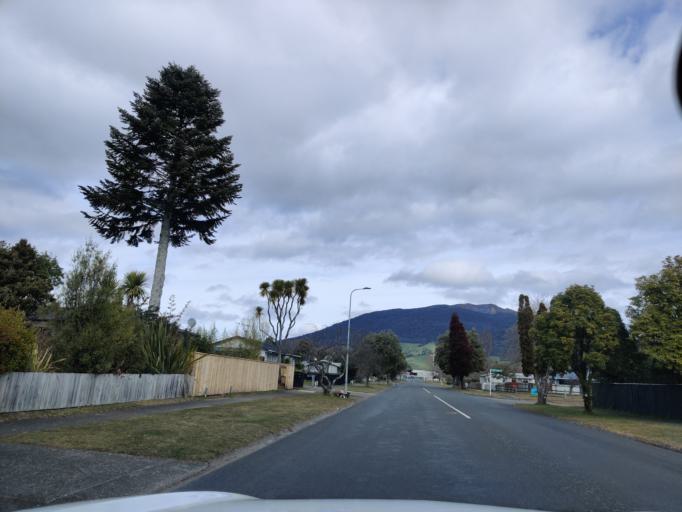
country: NZ
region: Waikato
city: Turangi
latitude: -38.9925
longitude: 175.8042
